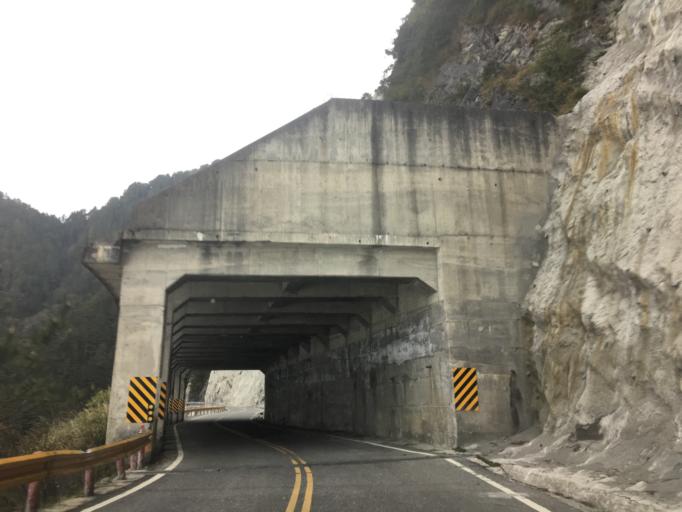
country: TW
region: Taiwan
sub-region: Hualien
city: Hualian
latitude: 24.1745
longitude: 121.3780
